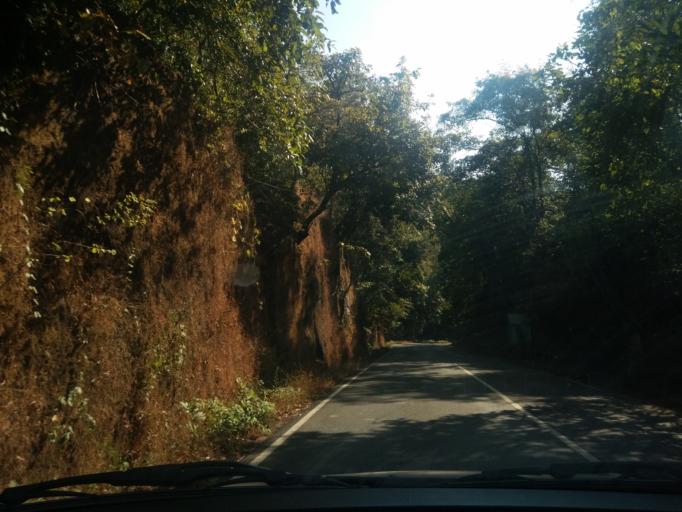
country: IN
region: Goa
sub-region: South Goa
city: Quepem
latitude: 15.1584
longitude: 74.1158
